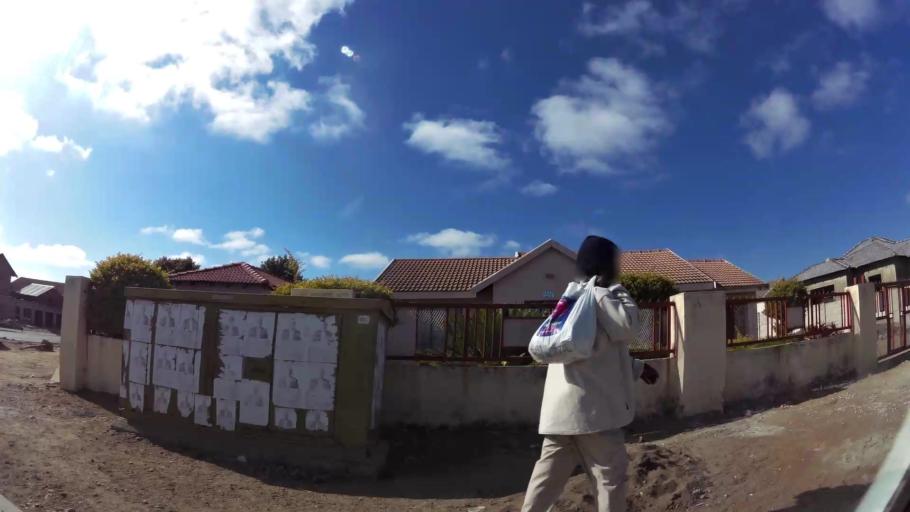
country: ZA
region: Limpopo
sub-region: Capricorn District Municipality
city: Polokwane
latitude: -23.8554
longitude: 29.3727
